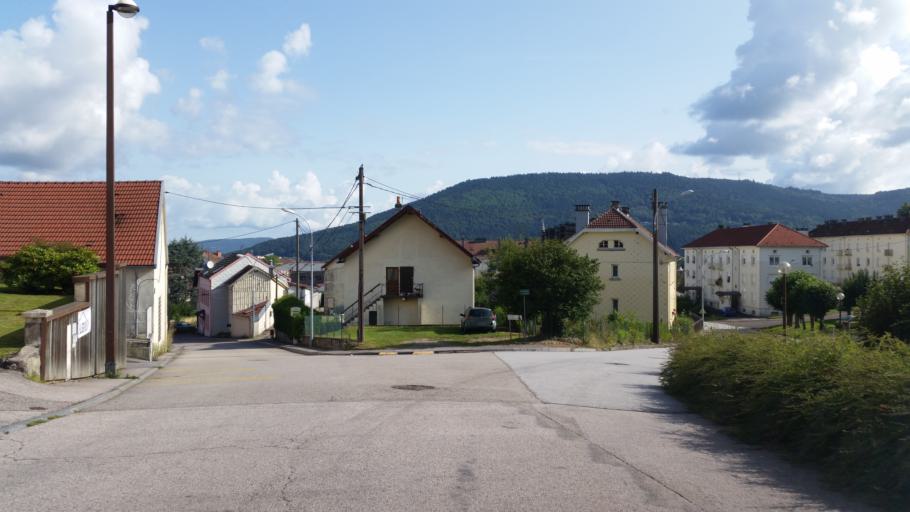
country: FR
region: Lorraine
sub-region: Departement des Vosges
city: Remiremont
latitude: 48.0111
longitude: 6.5863
